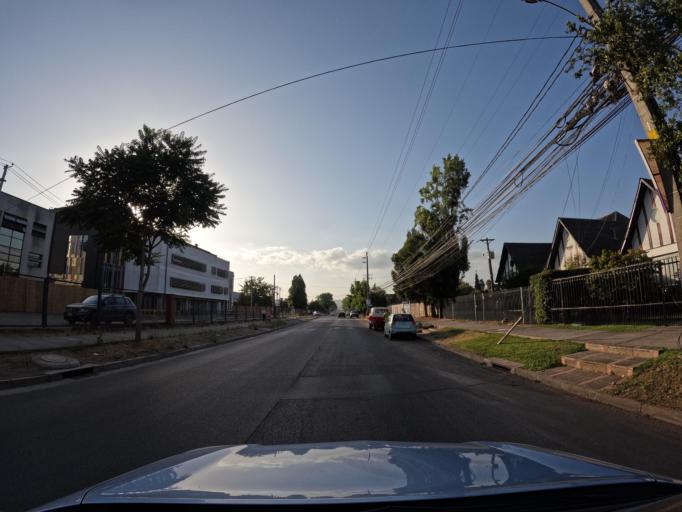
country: CL
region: Maule
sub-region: Provincia de Talca
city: Talca
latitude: -35.4340
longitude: -71.6191
